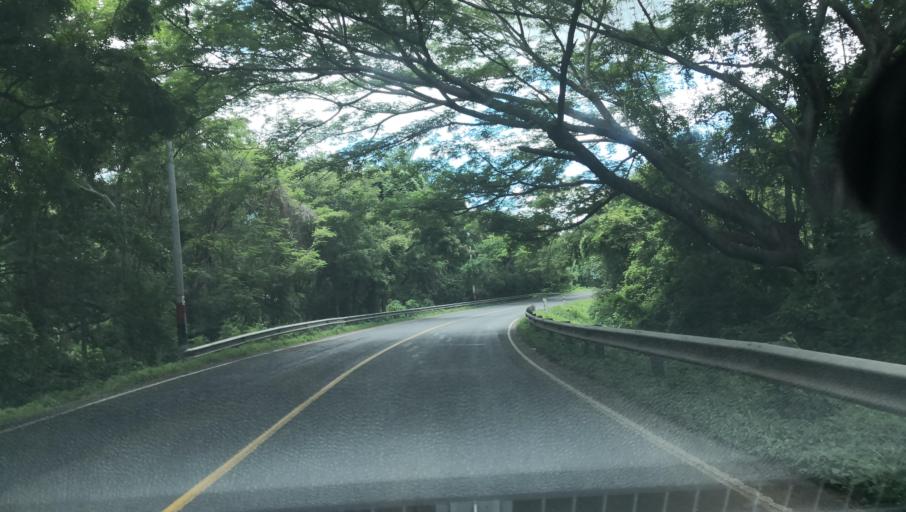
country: NI
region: Madriz
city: Yalaguina
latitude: 13.4773
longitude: -86.4857
